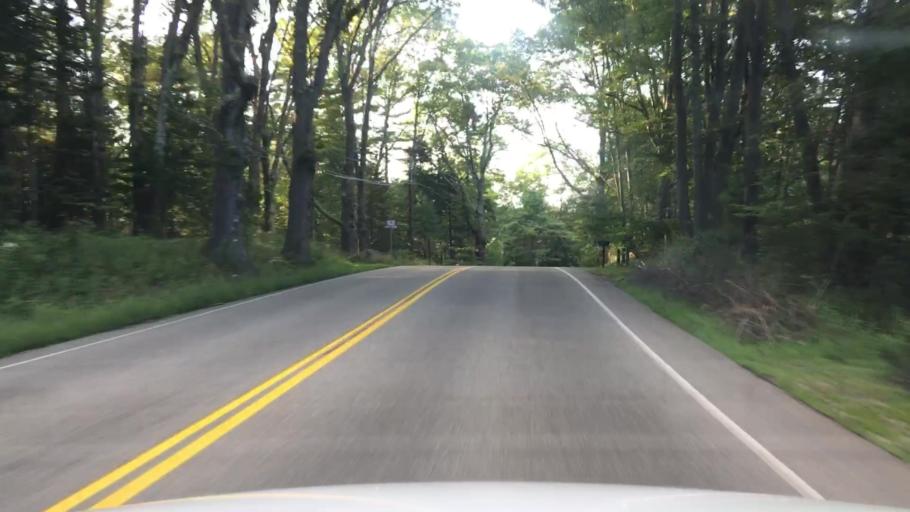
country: US
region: Maine
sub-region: Cumberland County
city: Scarborough
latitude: 43.5727
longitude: -70.2806
